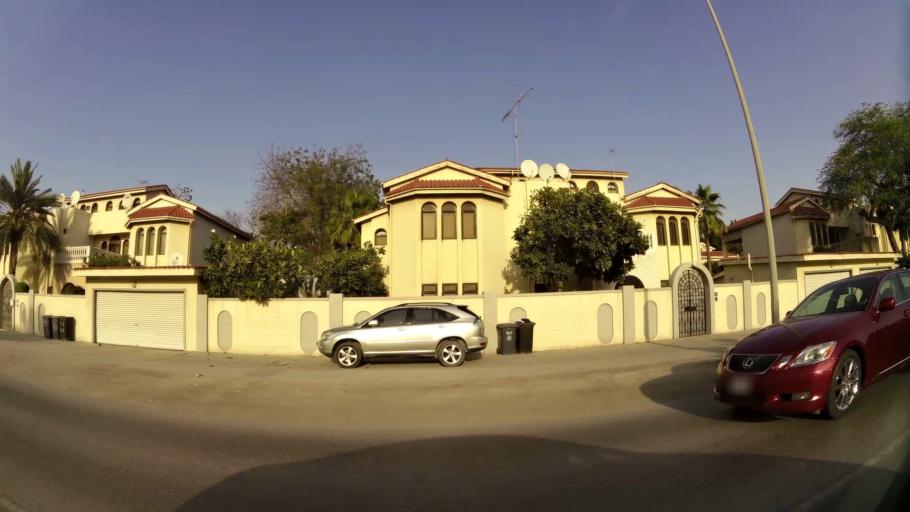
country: BH
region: Manama
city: Jidd Hafs
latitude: 26.2007
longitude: 50.4848
